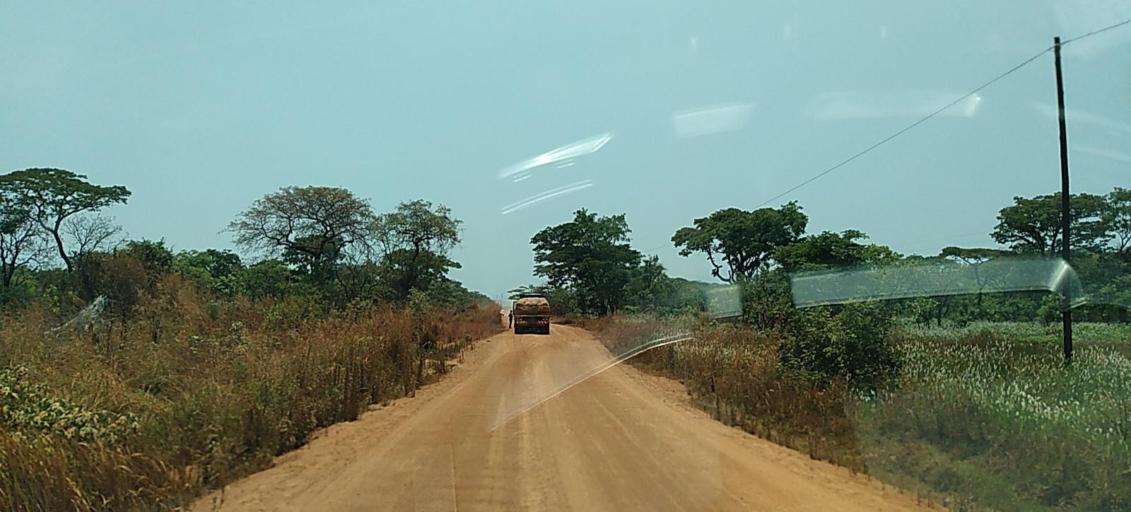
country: CD
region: Katanga
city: Kipushi
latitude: -11.9267
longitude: 26.9987
